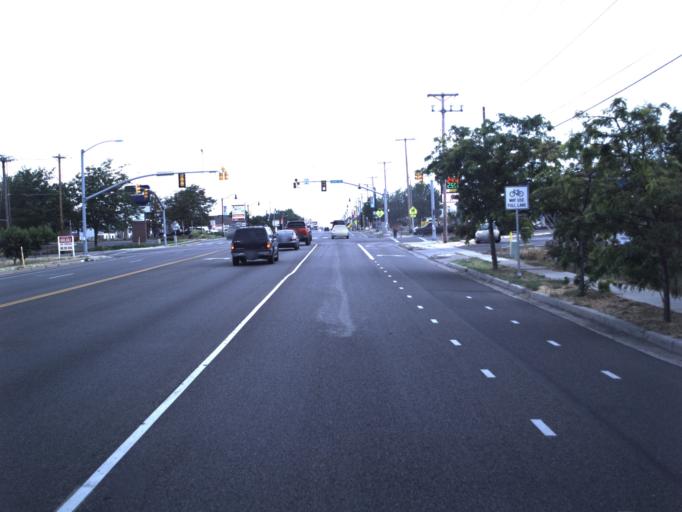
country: US
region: Utah
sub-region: Weber County
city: Roy
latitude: 41.1770
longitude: -112.0261
